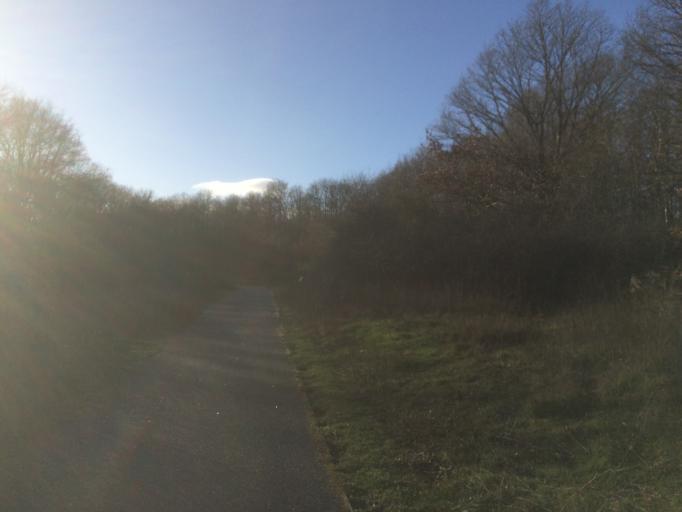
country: FR
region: Ile-de-France
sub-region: Departement de l'Essonne
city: Igny
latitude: 48.7406
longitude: 2.2204
